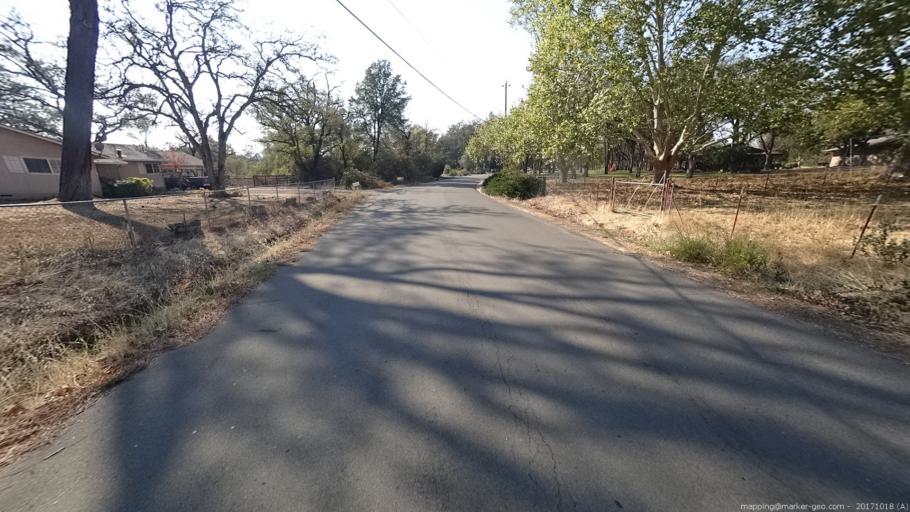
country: US
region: California
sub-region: Shasta County
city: Palo Cedro
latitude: 40.5725
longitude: -122.2362
